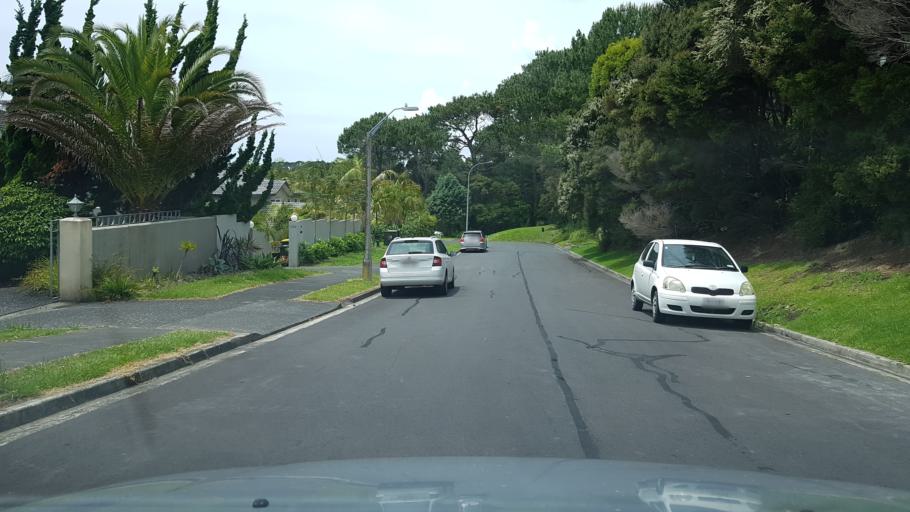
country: NZ
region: Auckland
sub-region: Auckland
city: North Shore
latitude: -36.8219
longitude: 174.7149
